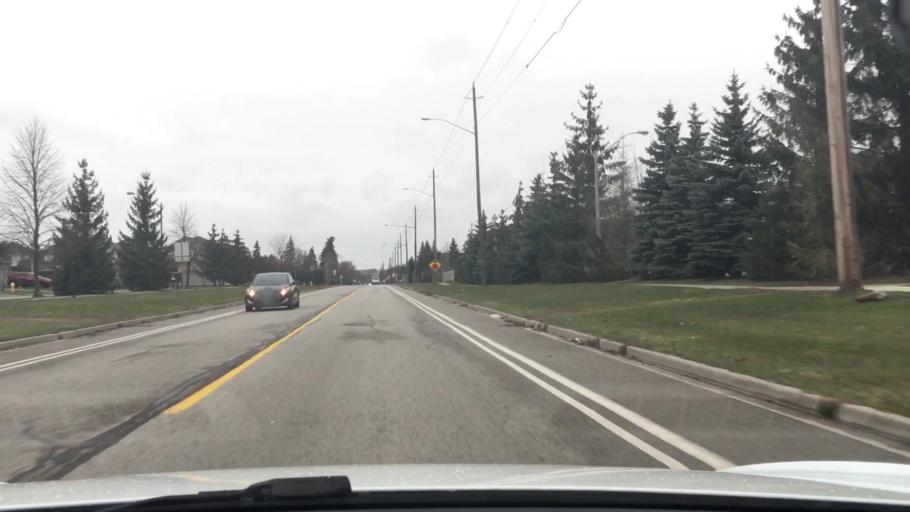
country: CA
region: Ontario
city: Oshawa
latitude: 43.9013
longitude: -78.7840
